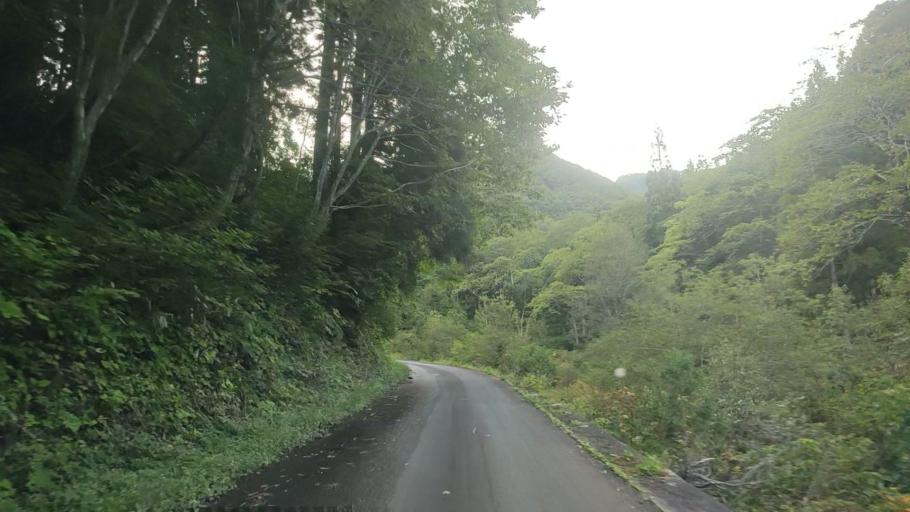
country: JP
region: Toyama
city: Yatsuomachi-higashikumisaka
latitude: 36.3304
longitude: 137.0765
